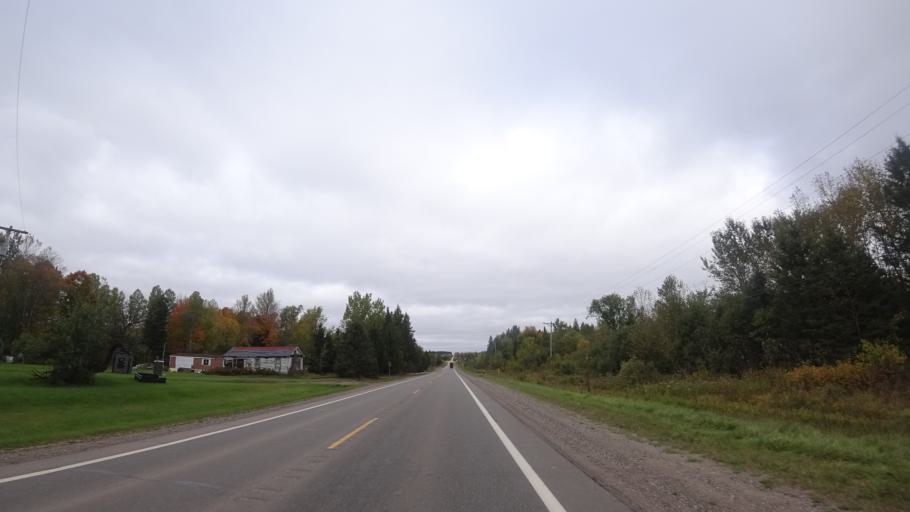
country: US
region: Wisconsin
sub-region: Florence County
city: Florence
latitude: 46.0993
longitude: -88.0757
